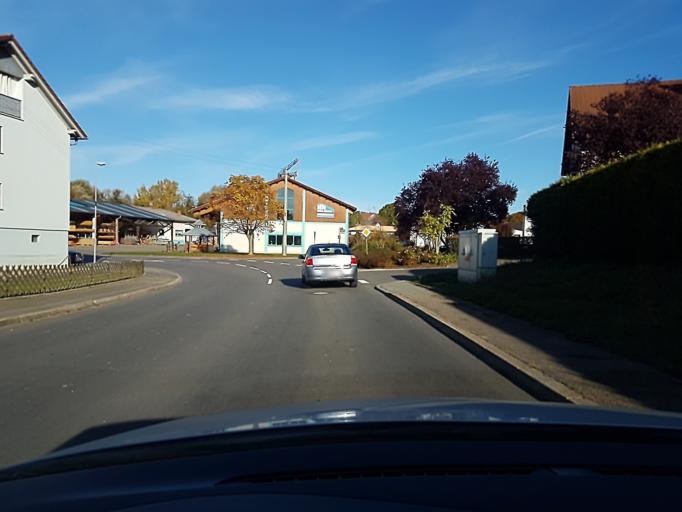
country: DE
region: Baden-Wuerttemberg
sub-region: Karlsruhe Region
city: Billigheim
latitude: 49.3516
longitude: 9.2235
